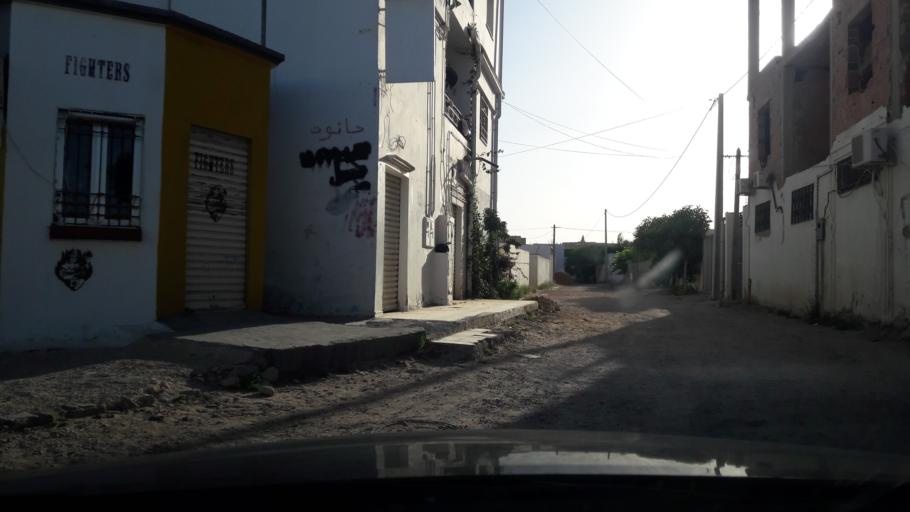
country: TN
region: Safaqis
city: Al Qarmadah
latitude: 34.7965
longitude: 10.7606
